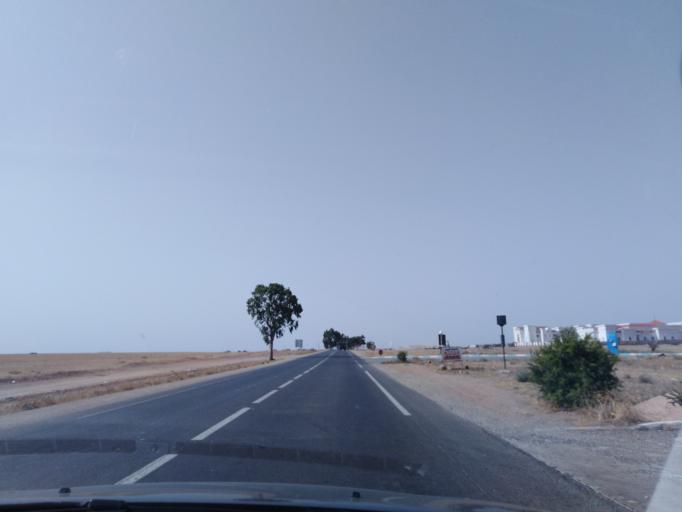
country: MA
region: Marrakech-Tensift-Al Haouz
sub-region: Kelaa-Des-Sraghna
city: Sidi Bou Othmane
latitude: 32.2177
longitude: -7.9569
